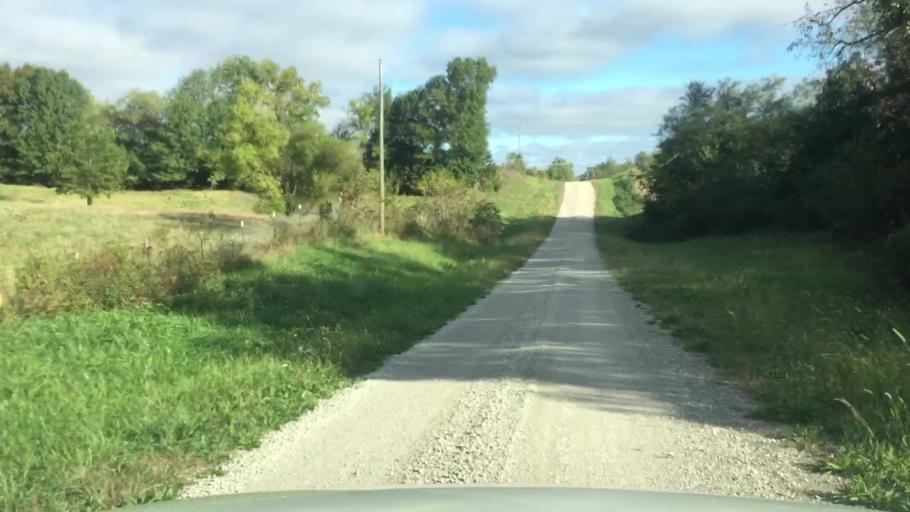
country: US
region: Missouri
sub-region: Howard County
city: New Franklin
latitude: 39.0970
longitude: -92.7795
